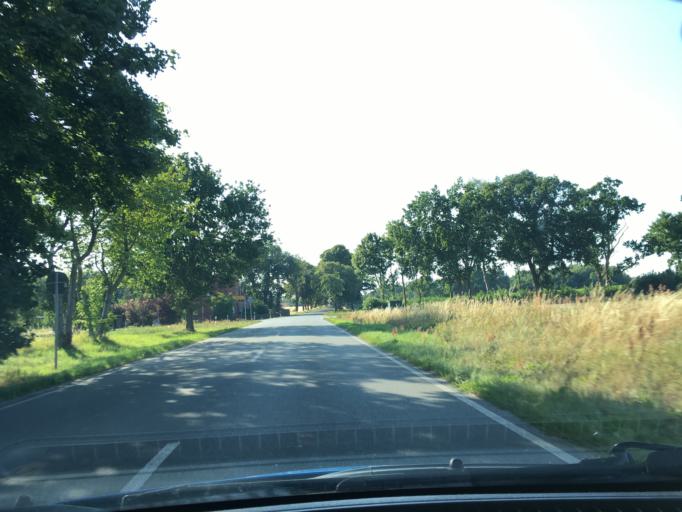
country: DE
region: Lower Saxony
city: Dahlem
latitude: 53.1800
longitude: 10.7602
